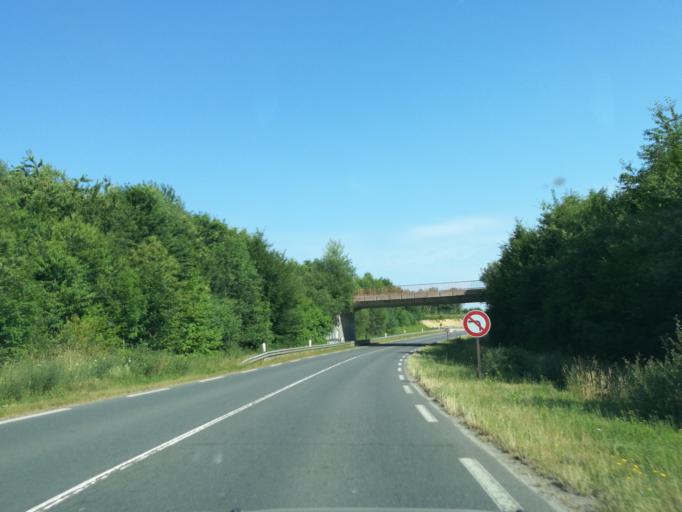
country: FR
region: Brittany
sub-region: Departement d'Ille-et-Vilaine
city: Montfort-sur-Meu
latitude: 48.1490
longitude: -1.9455
